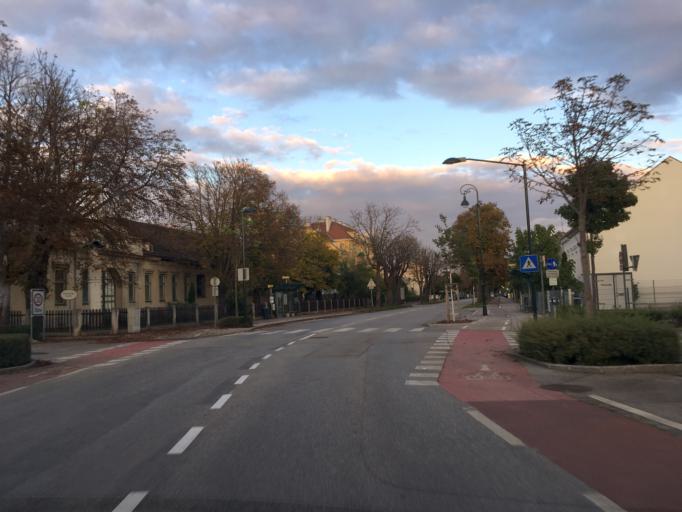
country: AT
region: Lower Austria
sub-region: Politischer Bezirk Baden
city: Baden
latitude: 48.0111
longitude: 16.2442
